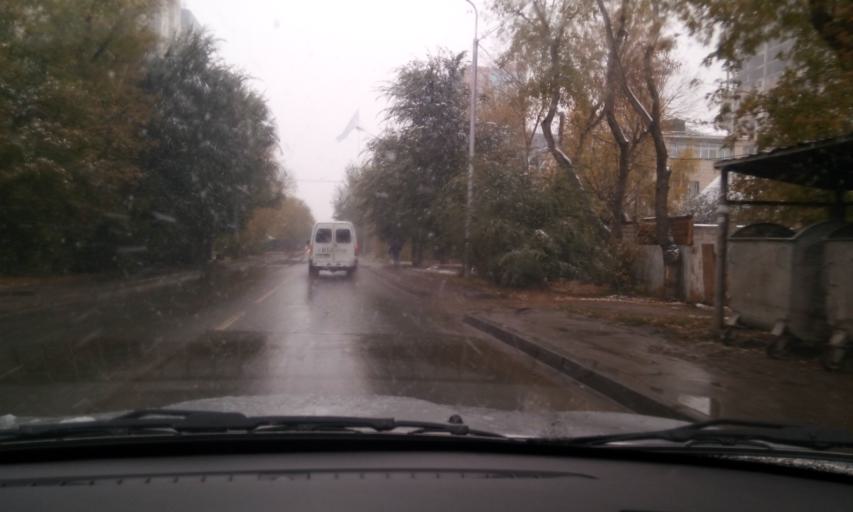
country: KZ
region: Astana Qalasy
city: Astana
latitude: 51.1452
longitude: 71.4267
